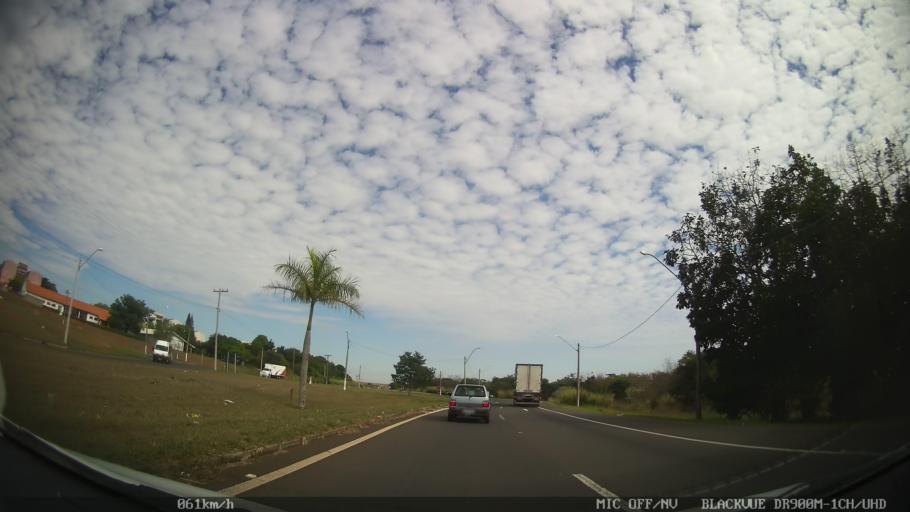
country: BR
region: Sao Paulo
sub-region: Santa Barbara D'Oeste
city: Santa Barbara d'Oeste
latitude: -22.7720
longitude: -47.4241
